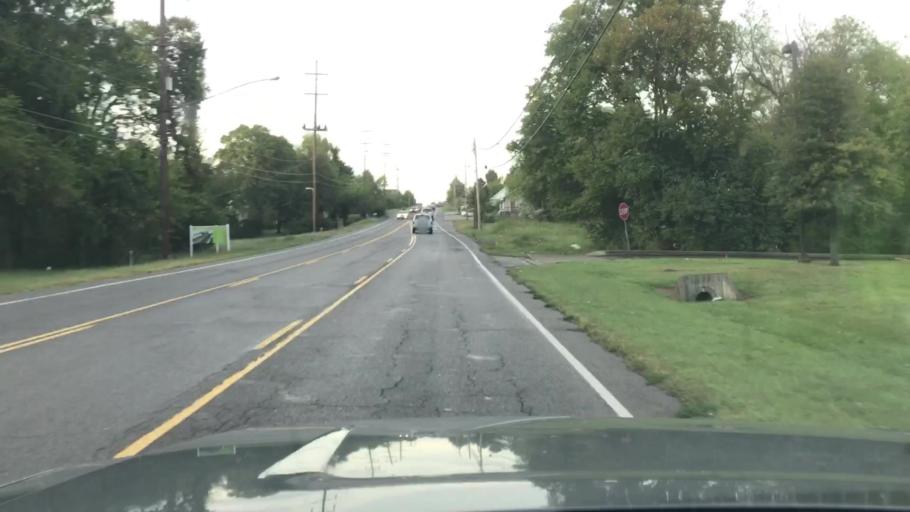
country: US
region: Tennessee
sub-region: Davidson County
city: Nashville
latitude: 36.2116
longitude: -86.8388
